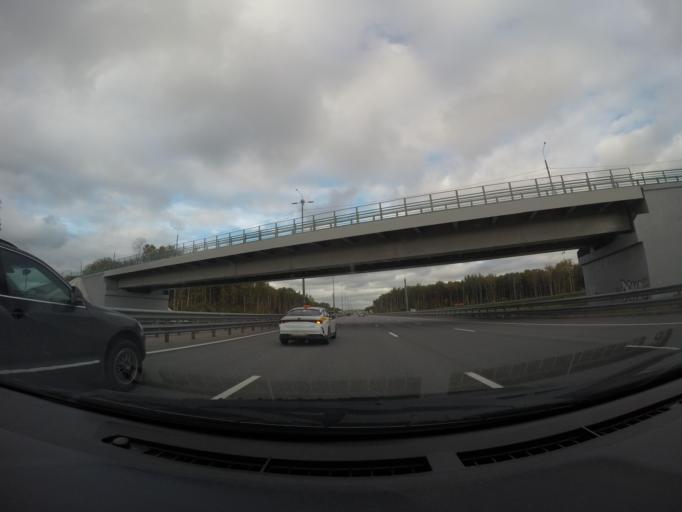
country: RU
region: Moskovskaya
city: Barvikha
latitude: 55.7113
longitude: 37.3142
